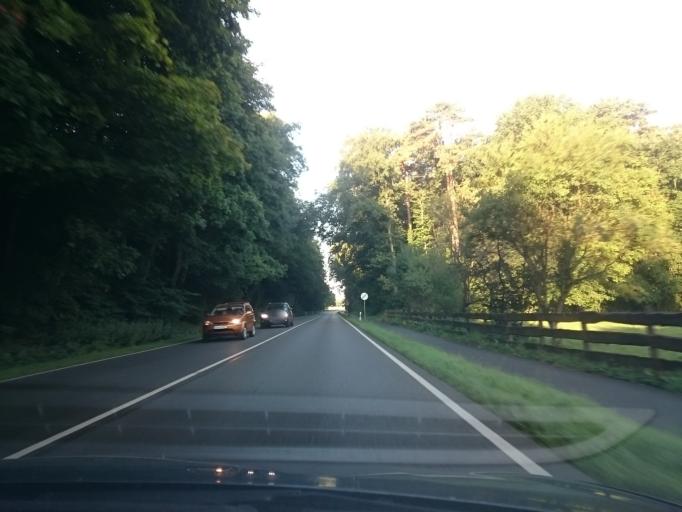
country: DE
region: Mecklenburg-Vorpommern
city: Karlshagen
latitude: 54.0630
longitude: 13.8362
